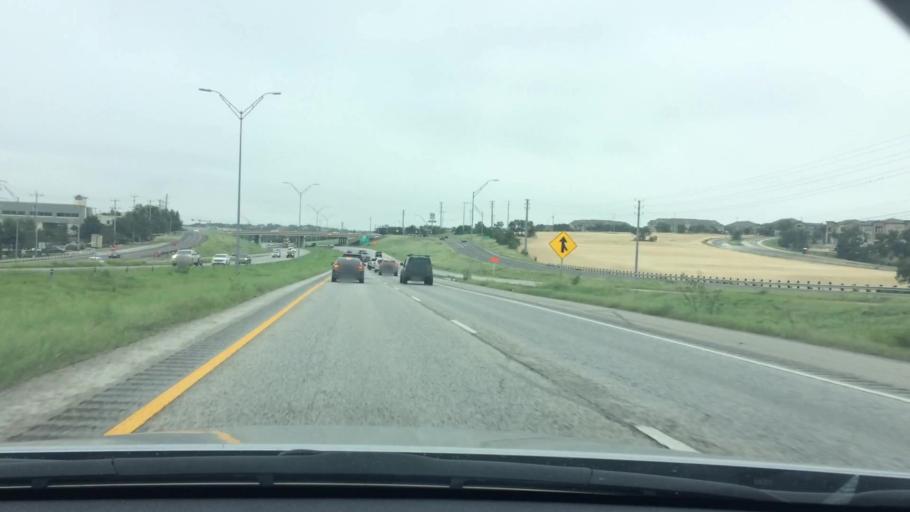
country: US
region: Texas
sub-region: Bexar County
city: Leon Valley
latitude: 29.4541
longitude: -98.6873
